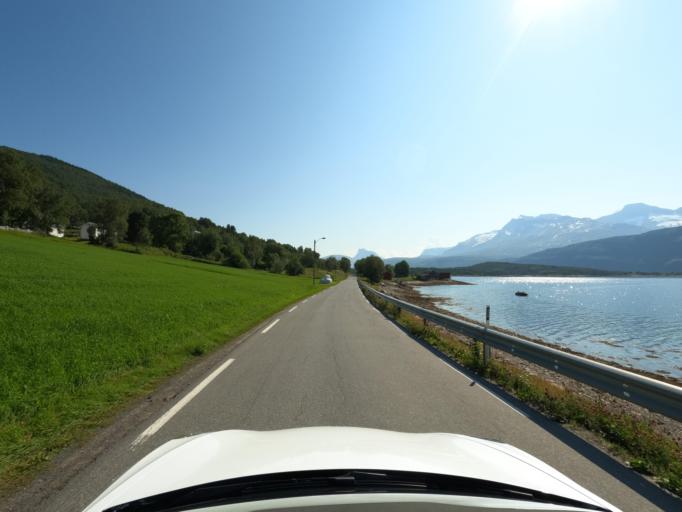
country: NO
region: Nordland
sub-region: Narvik
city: Narvik
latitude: 68.3354
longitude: 17.2767
